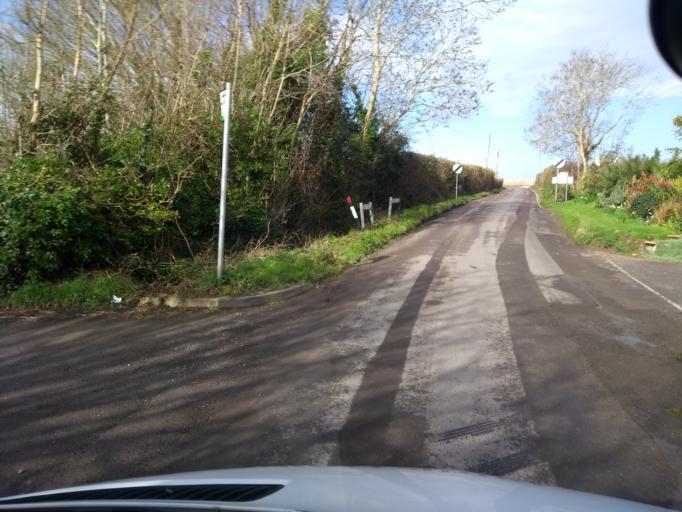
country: GB
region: England
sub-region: Somerset
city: Woolavington
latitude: 51.1605
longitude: -2.9263
